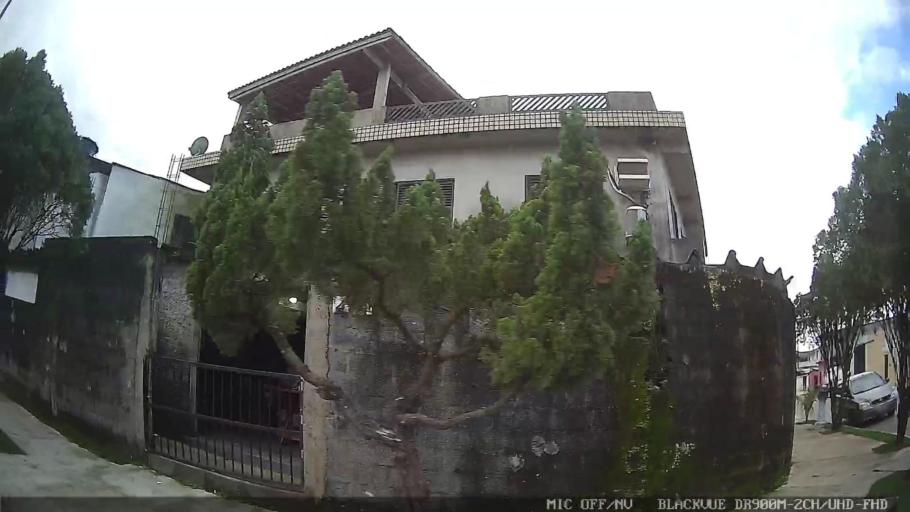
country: BR
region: Sao Paulo
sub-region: Guaruja
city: Guaruja
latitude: -23.9983
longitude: -46.2910
